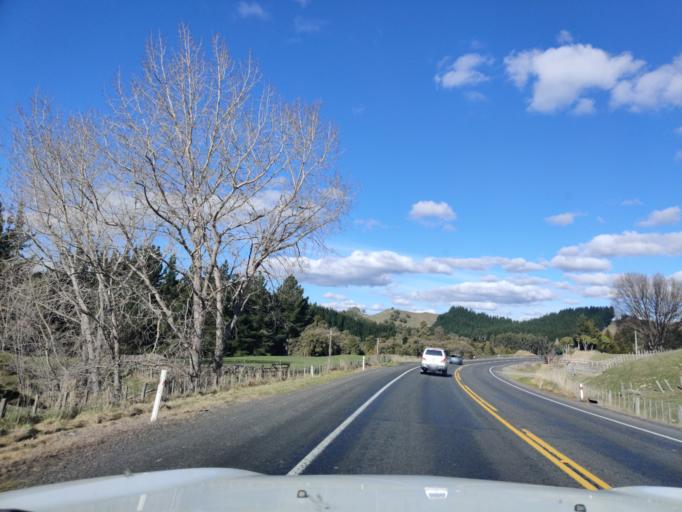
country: NZ
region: Manawatu-Wanganui
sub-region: Ruapehu District
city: Waiouru
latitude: -39.6172
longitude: 175.7614
